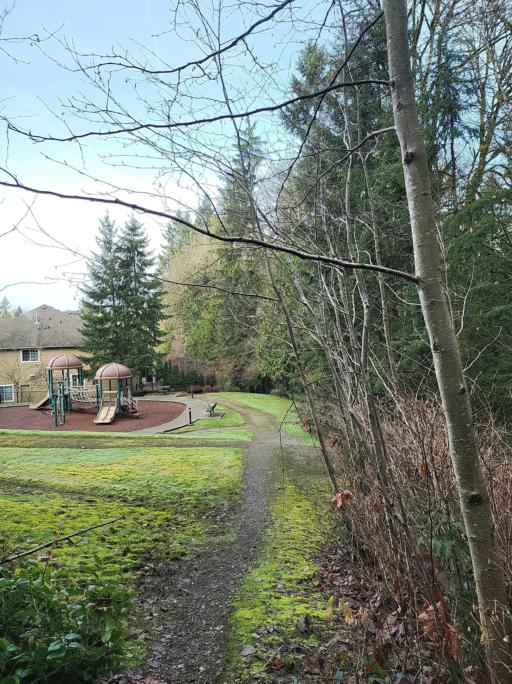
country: US
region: Washington
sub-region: King County
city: Newcastle
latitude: 47.5283
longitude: -122.1380
